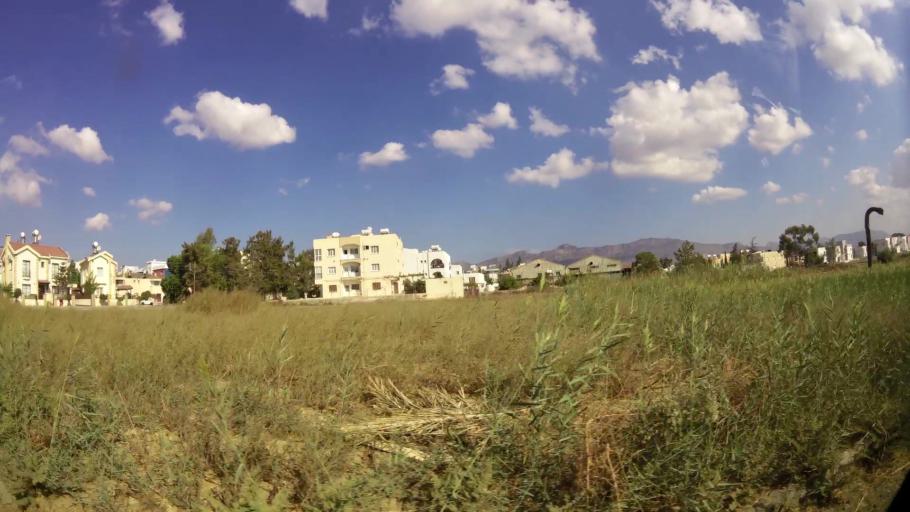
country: CY
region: Lefkosia
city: Nicosia
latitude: 35.2146
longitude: 33.3799
